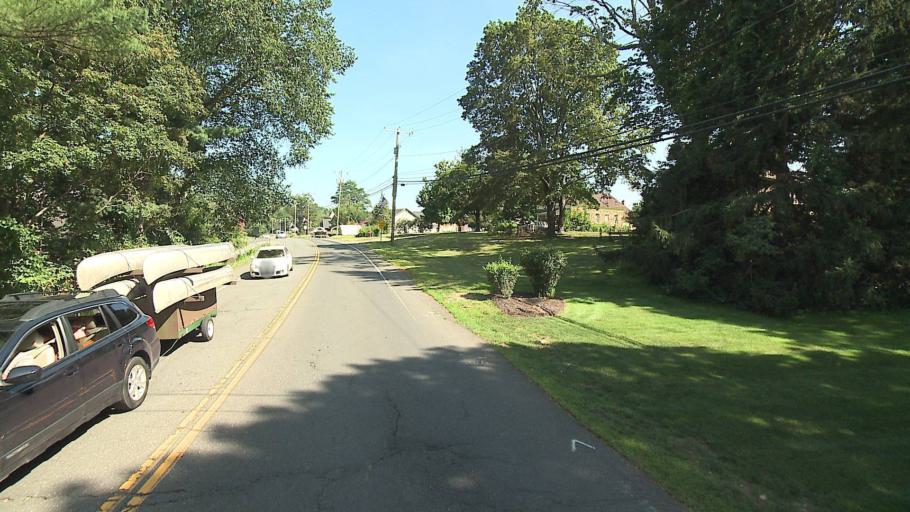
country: US
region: Connecticut
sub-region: Hartford County
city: West Simsbury
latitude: 41.8730
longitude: -72.8580
